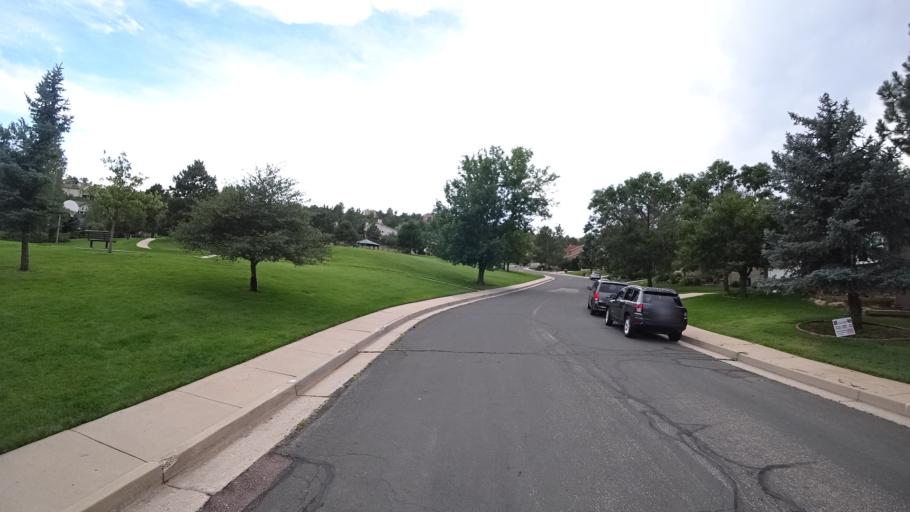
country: US
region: Colorado
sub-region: El Paso County
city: Colorado Springs
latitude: 38.9098
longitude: -104.8438
